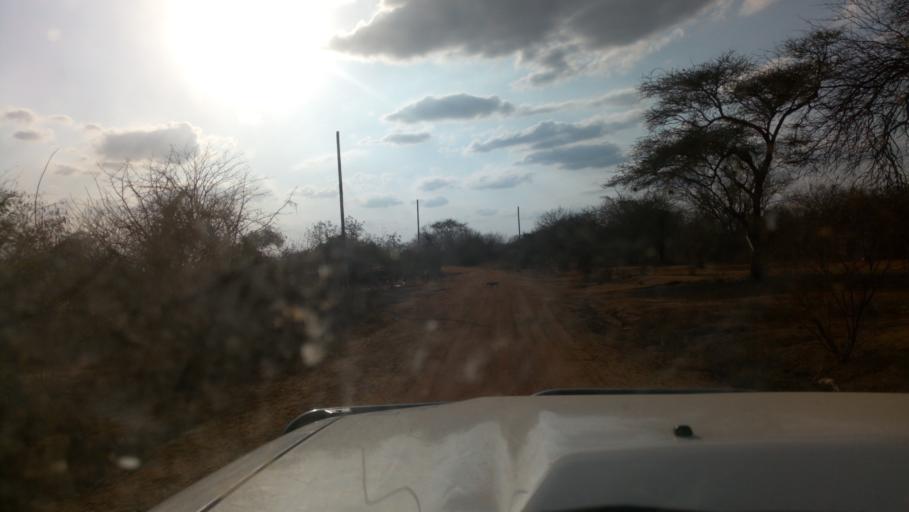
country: KE
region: Kitui
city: Kitui
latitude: -1.6894
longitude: 38.3515
